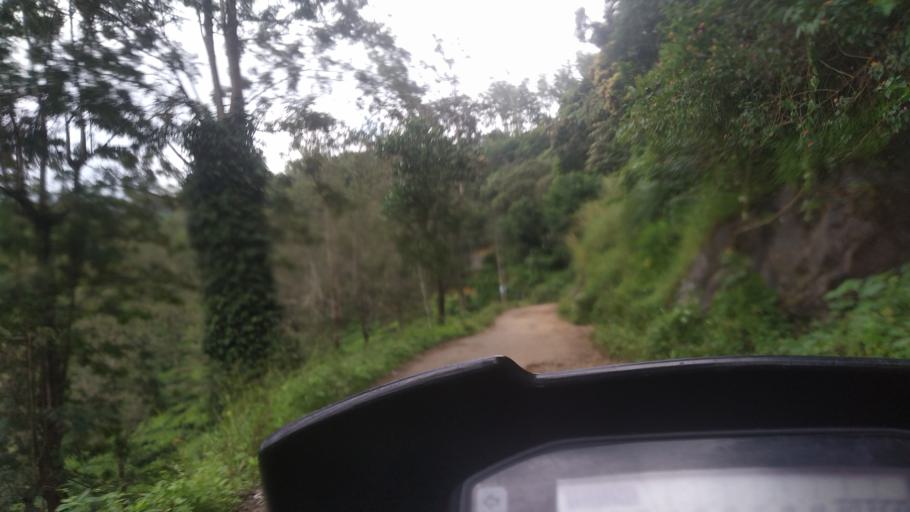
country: IN
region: Tamil Nadu
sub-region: Theni
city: Gudalur
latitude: 9.5746
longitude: 77.0827
